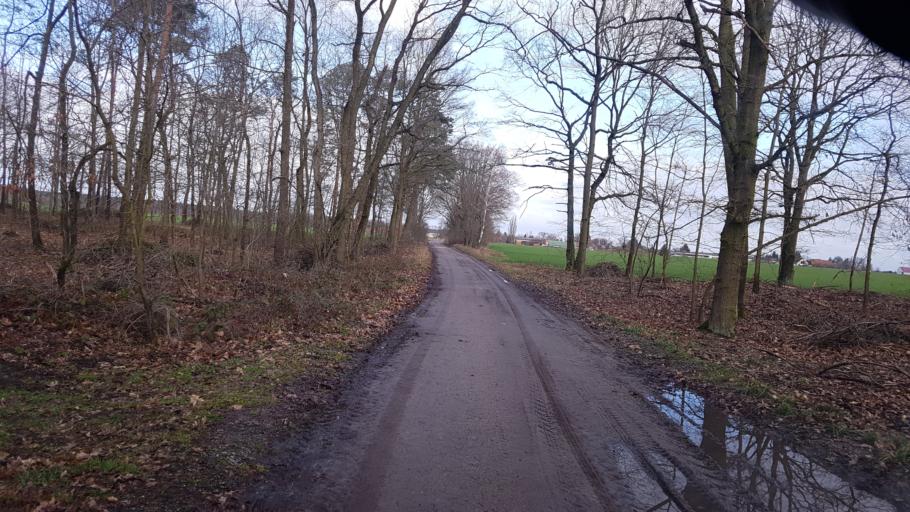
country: DE
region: Brandenburg
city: Finsterwalde
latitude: 51.5968
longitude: 13.6715
